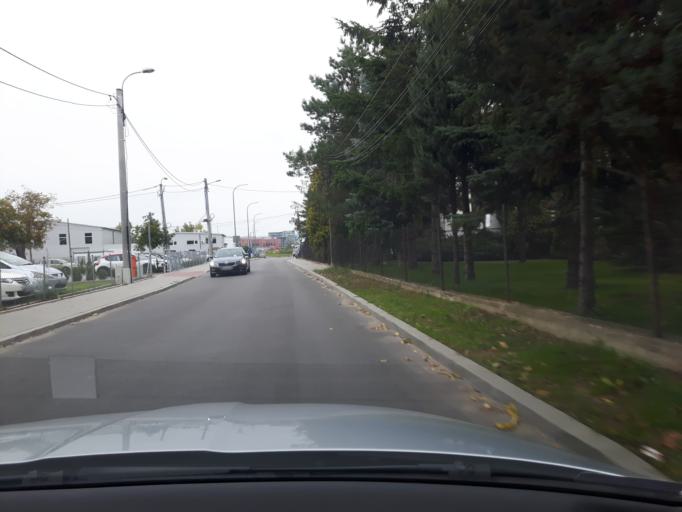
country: PL
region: Masovian Voivodeship
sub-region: Warszawa
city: Wlochy
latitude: 52.1967
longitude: 20.9382
